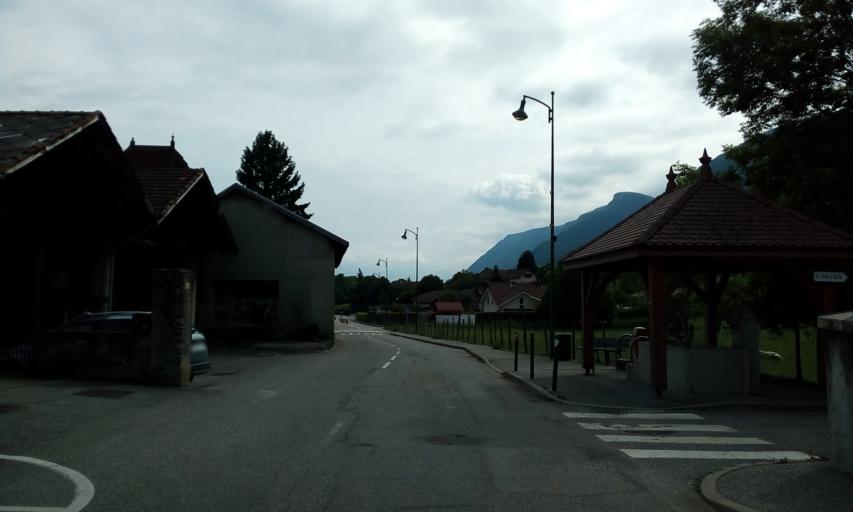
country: FR
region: Rhone-Alpes
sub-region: Departement de l'Isere
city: Saint-Vincent-de-Mercuze
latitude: 45.3966
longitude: 5.9624
